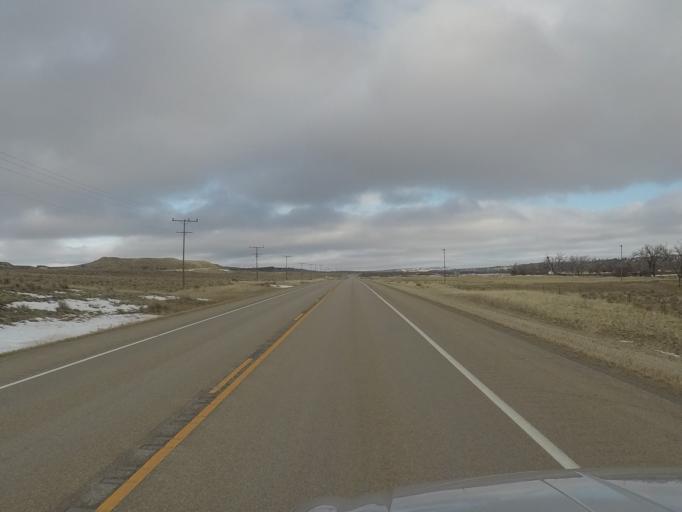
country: US
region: Montana
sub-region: Golden Valley County
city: Ryegate
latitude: 46.3142
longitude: -109.3797
